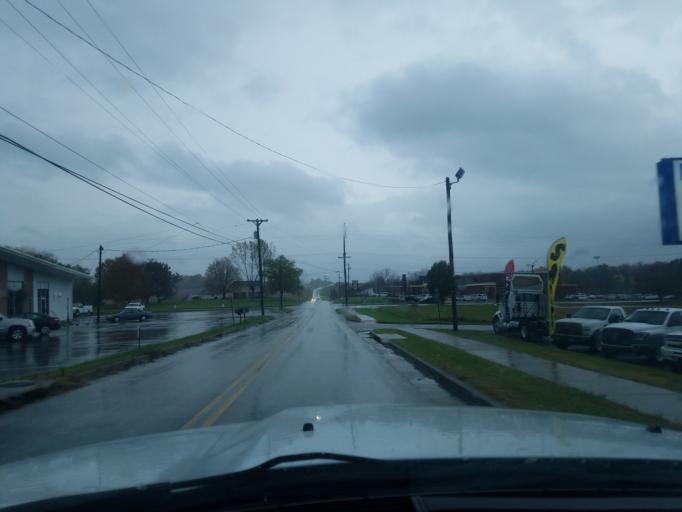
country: US
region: Kentucky
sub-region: Taylor County
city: Campbellsville
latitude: 37.3506
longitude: -85.3314
